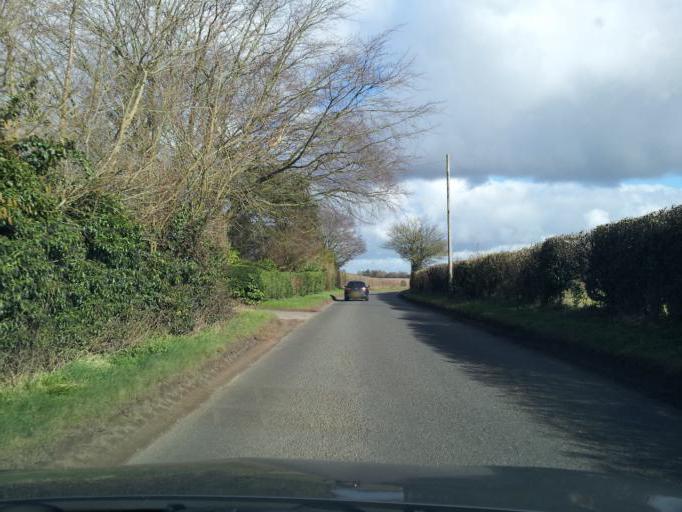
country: GB
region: England
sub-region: Norfolk
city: Mattishall
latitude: 52.6593
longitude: 1.0589
